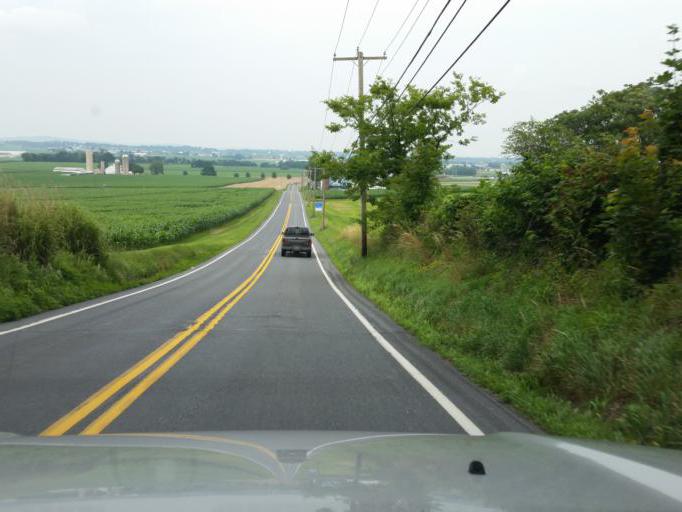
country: US
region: Pennsylvania
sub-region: Lancaster County
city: Manheim
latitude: 40.1540
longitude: -76.3675
